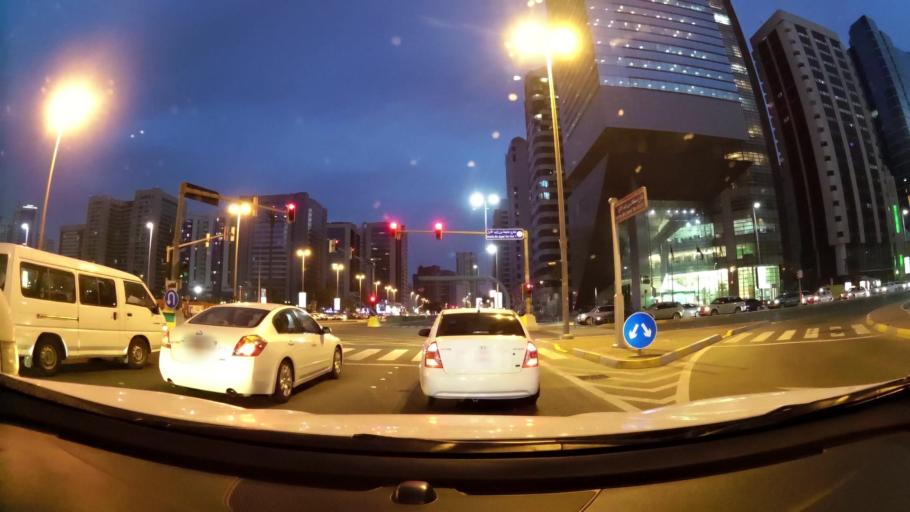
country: AE
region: Abu Dhabi
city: Abu Dhabi
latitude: 24.4923
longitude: 54.3612
